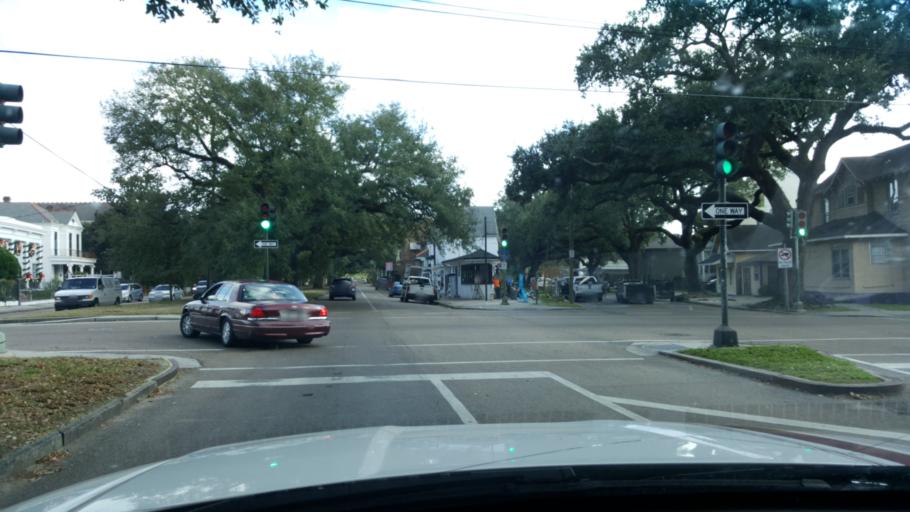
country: US
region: Louisiana
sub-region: Orleans Parish
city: New Orleans
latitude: 29.9726
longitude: -90.0733
